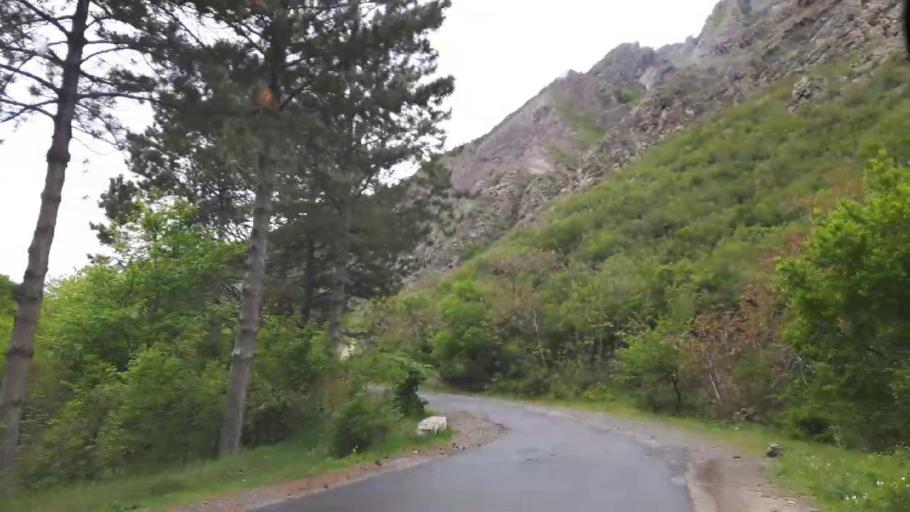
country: GE
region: Shida Kartli
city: Gori
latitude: 41.9004
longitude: 44.0736
